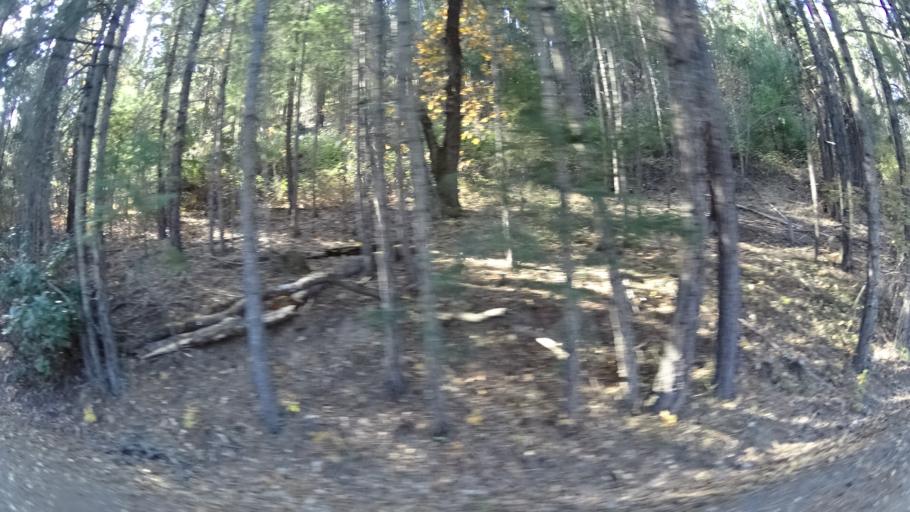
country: US
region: California
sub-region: Siskiyou County
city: Yreka
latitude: 41.8223
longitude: -122.9749
